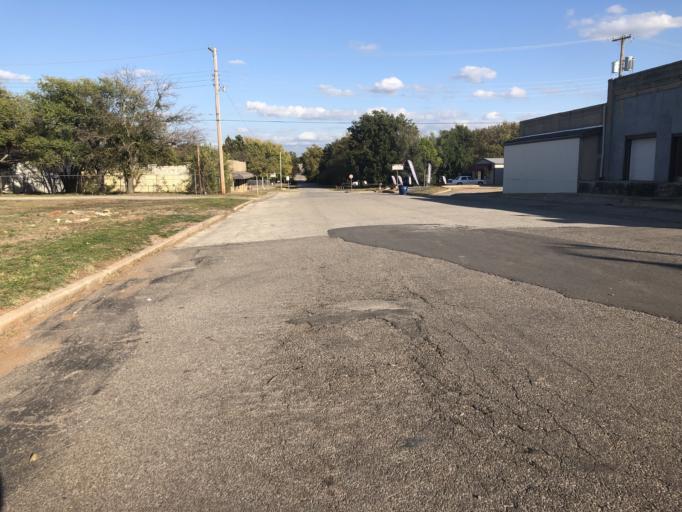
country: US
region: Oklahoma
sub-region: Pottawatomie County
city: Tecumseh
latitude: 35.2587
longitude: -96.9366
